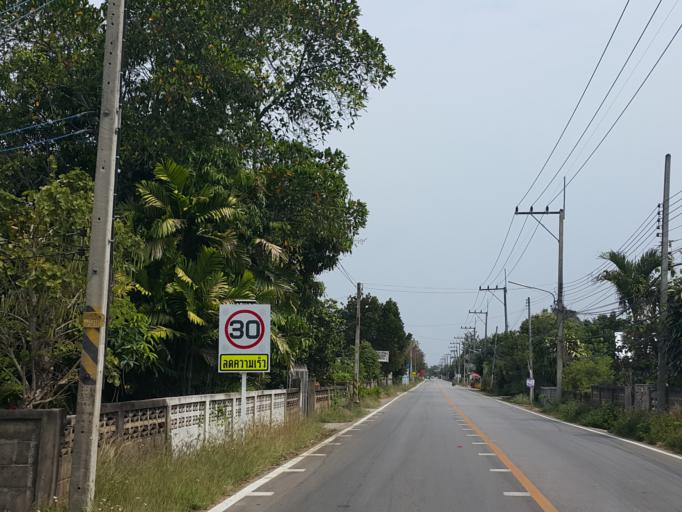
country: TH
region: Lampang
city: Ko Kha
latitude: 18.1707
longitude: 99.3879
